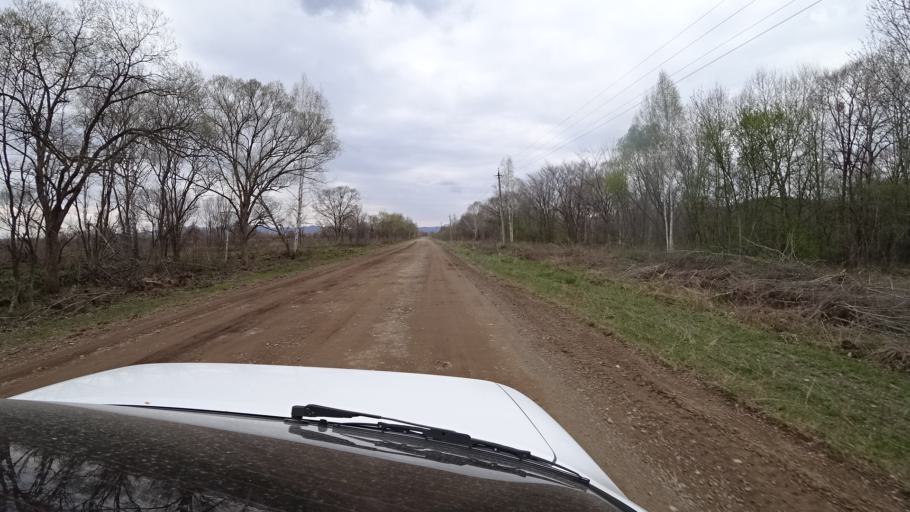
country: RU
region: Primorskiy
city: Novopokrovka
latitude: 45.5596
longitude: 134.3460
